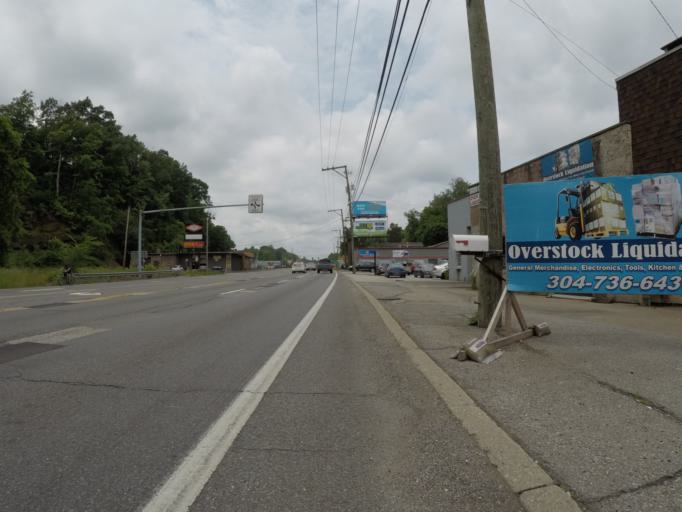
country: US
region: West Virginia
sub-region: Cabell County
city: Pea Ridge
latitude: 38.4130
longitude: -82.3583
